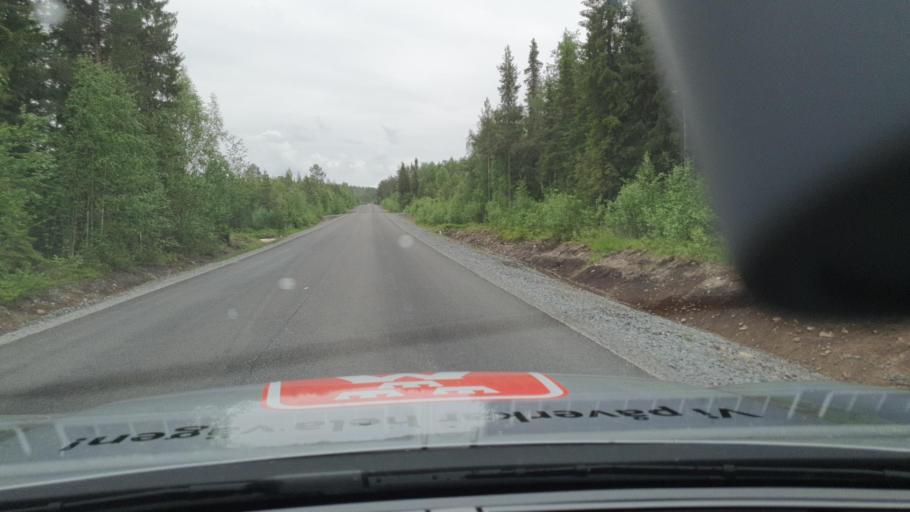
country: SE
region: Norrbotten
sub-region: Overtornea Kommun
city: OEvertornea
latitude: 66.6079
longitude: 23.2957
